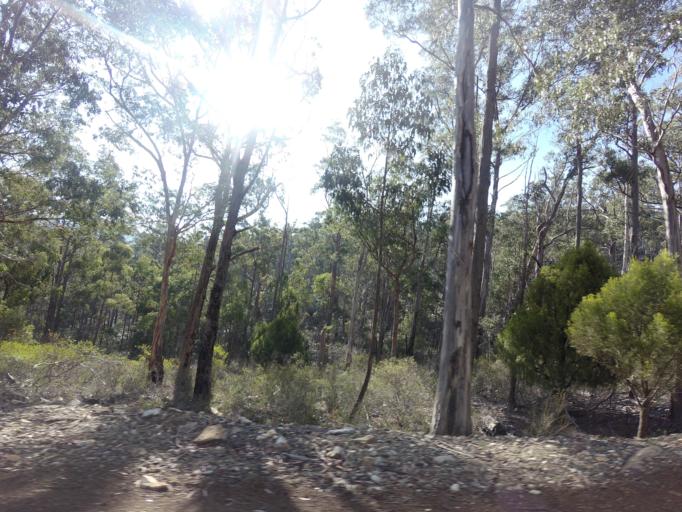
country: AU
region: Tasmania
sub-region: Sorell
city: Sorell
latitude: -42.5266
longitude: 147.4614
